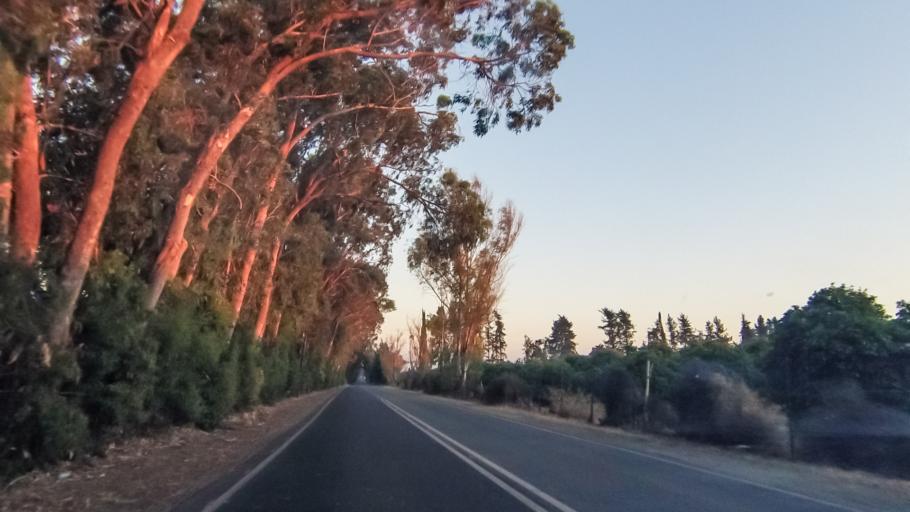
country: CY
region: Larnaka
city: Kolossi
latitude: 34.6513
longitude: 32.9420
